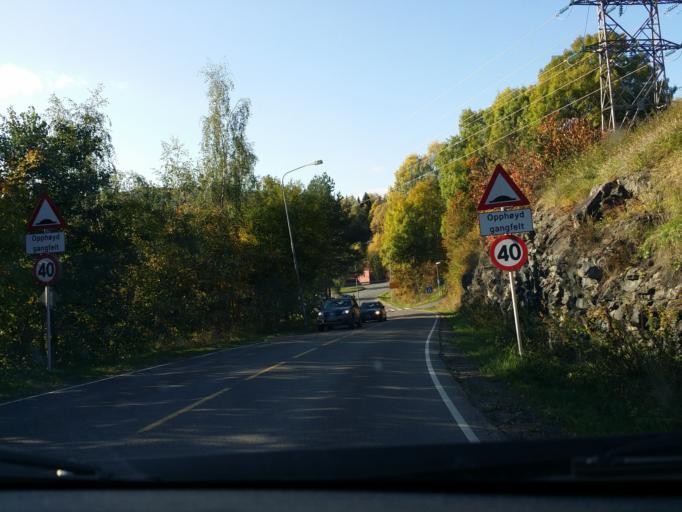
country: NO
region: Akershus
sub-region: Baerum
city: Sandvika
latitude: 59.9436
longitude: 10.5101
